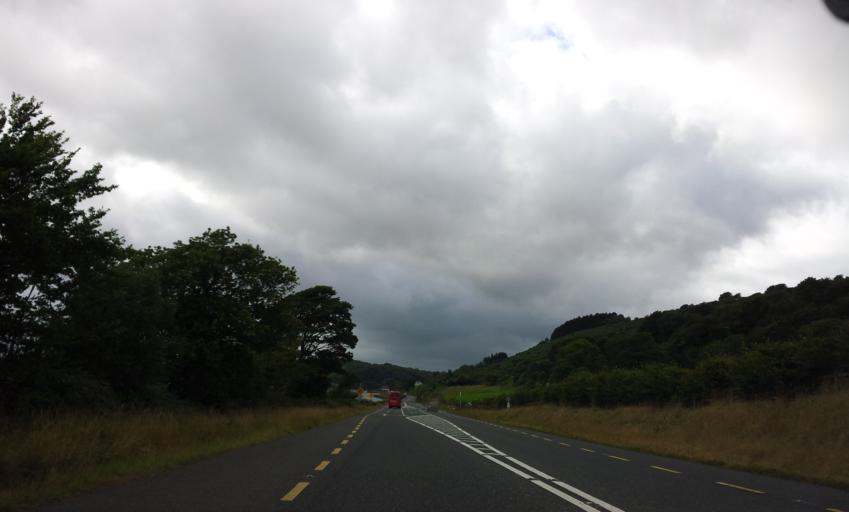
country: IE
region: Munster
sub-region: County Cork
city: Youghal
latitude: 51.9758
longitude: -7.8337
